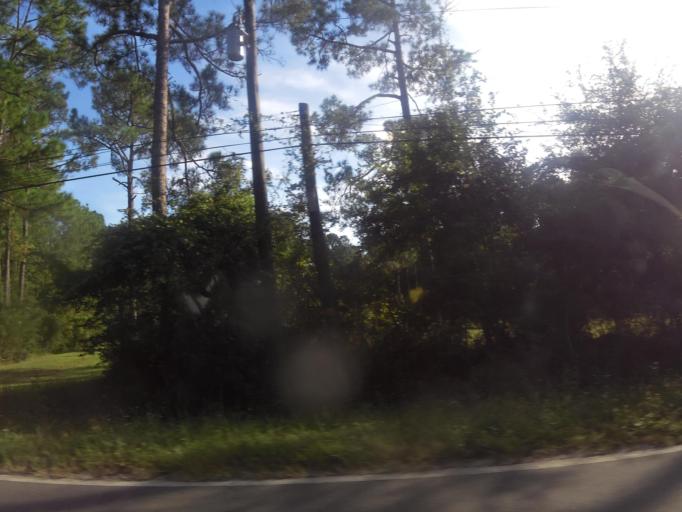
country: US
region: Florida
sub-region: Clay County
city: Green Cove Springs
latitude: 29.9146
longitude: -81.5327
